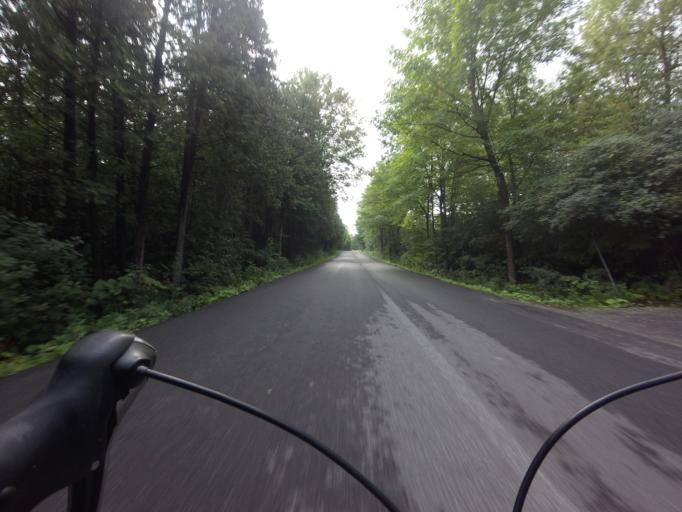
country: CA
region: Ontario
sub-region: Lanark County
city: Smiths Falls
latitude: 44.9574
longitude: -75.8005
